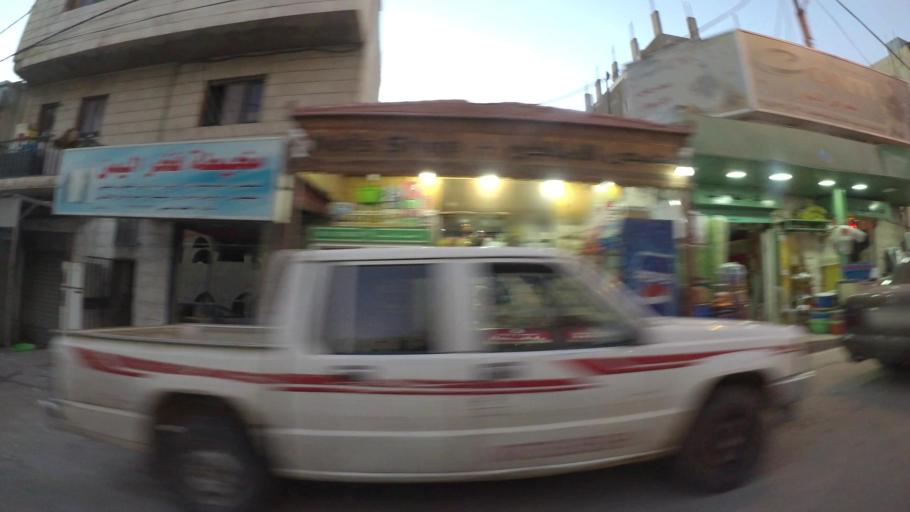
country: JO
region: Ma'an
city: Petra
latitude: 30.3214
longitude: 35.4800
